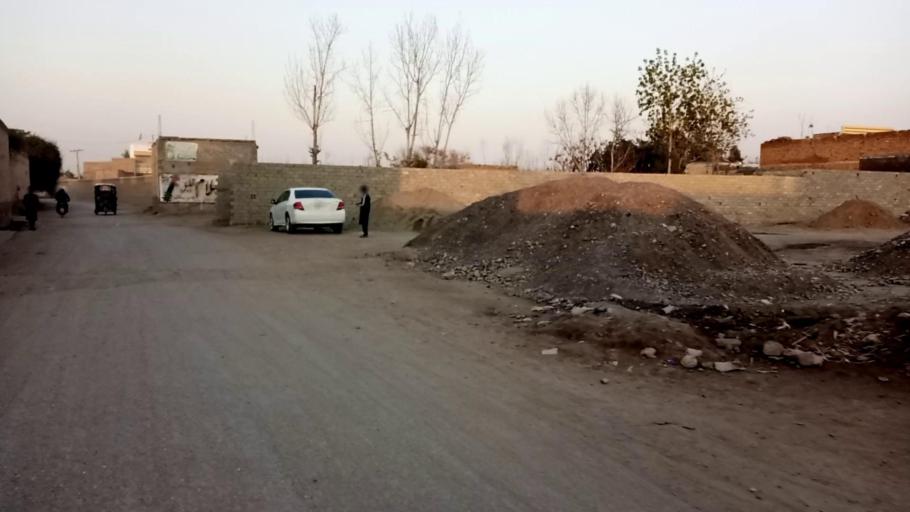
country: PK
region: Khyber Pakhtunkhwa
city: Peshawar
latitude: 34.0460
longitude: 71.4535
